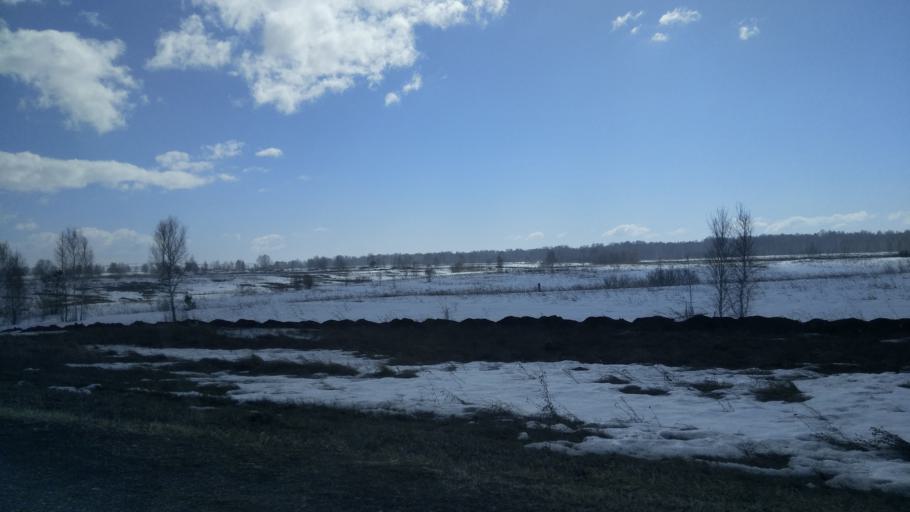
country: RU
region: Kemerovo
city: Yurga
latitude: 55.6836
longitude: 85.0165
